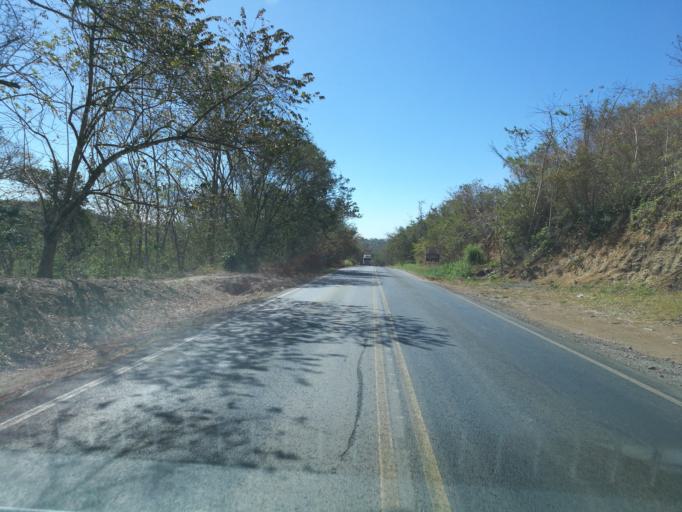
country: CR
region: Puntarenas
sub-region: Canton Central de Puntarenas
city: Puntarenas
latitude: 10.0927
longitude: -84.8547
